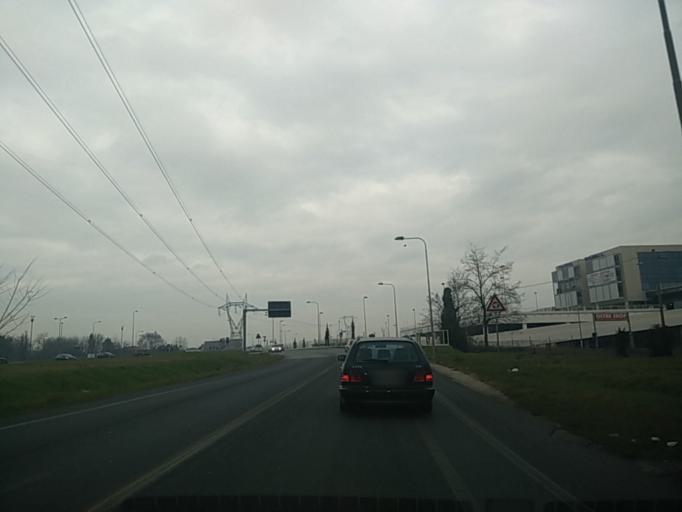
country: IT
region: Emilia-Romagna
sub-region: Provincia di Rimini
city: Santarcangelo
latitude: 44.0669
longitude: 12.4636
